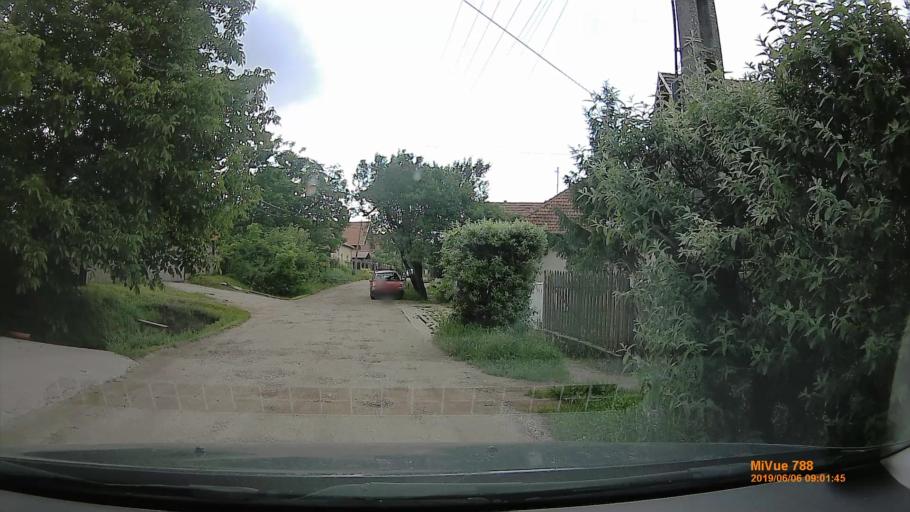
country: HU
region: Pest
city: Maglod
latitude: 47.4499
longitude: 19.3453
